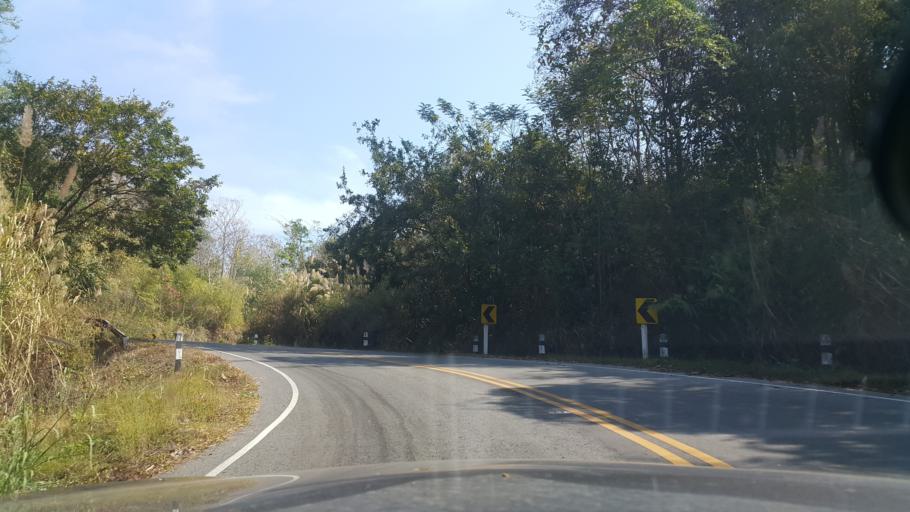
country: TH
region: Loei
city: Pak Chom
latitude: 18.0977
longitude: 102.0543
